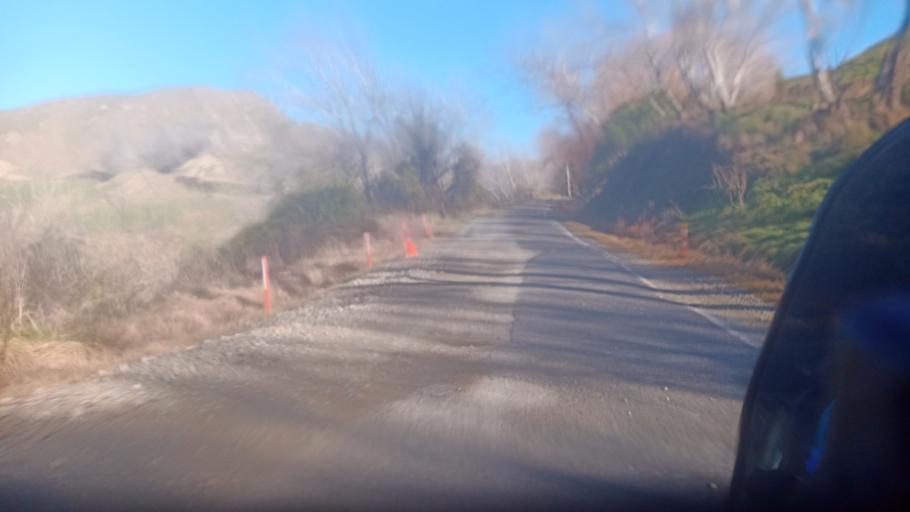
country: NZ
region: Gisborne
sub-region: Gisborne District
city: Gisborne
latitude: -38.5709
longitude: 177.5939
